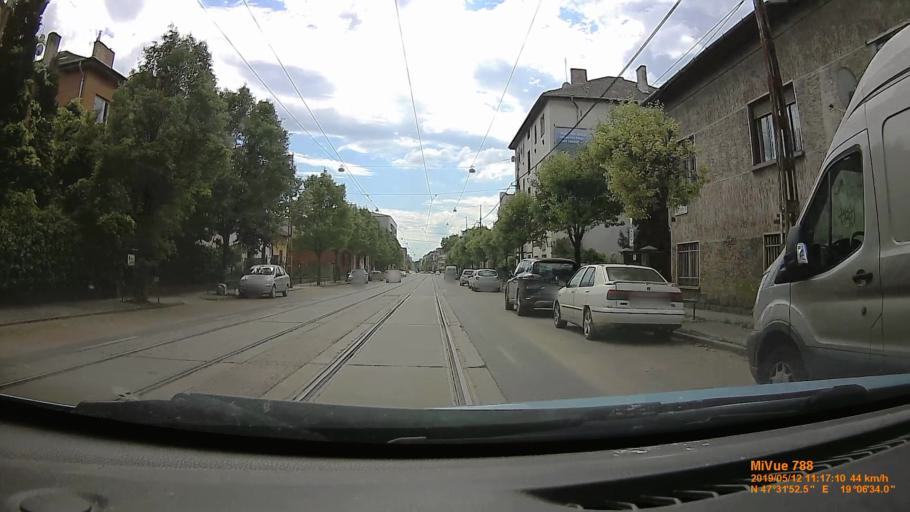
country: HU
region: Budapest
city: Budapest XIV. keruelet
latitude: 47.5312
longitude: 19.1094
